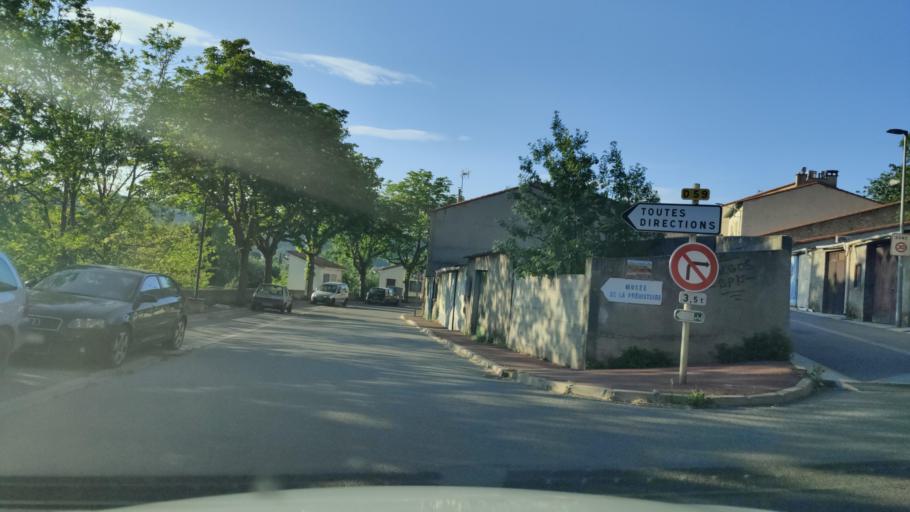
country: FR
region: Languedoc-Roussillon
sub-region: Departement des Pyrenees-Orientales
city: Estagel
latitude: 42.8108
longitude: 2.7444
